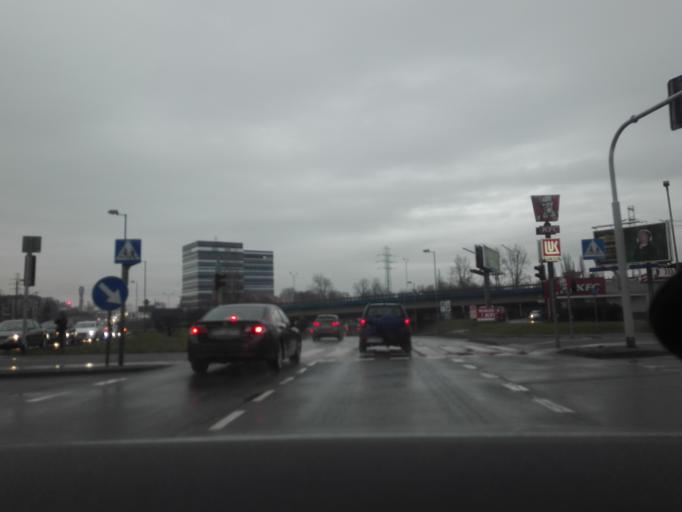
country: PL
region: Silesian Voivodeship
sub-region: Katowice
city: Katowice
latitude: 50.2719
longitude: 18.9920
